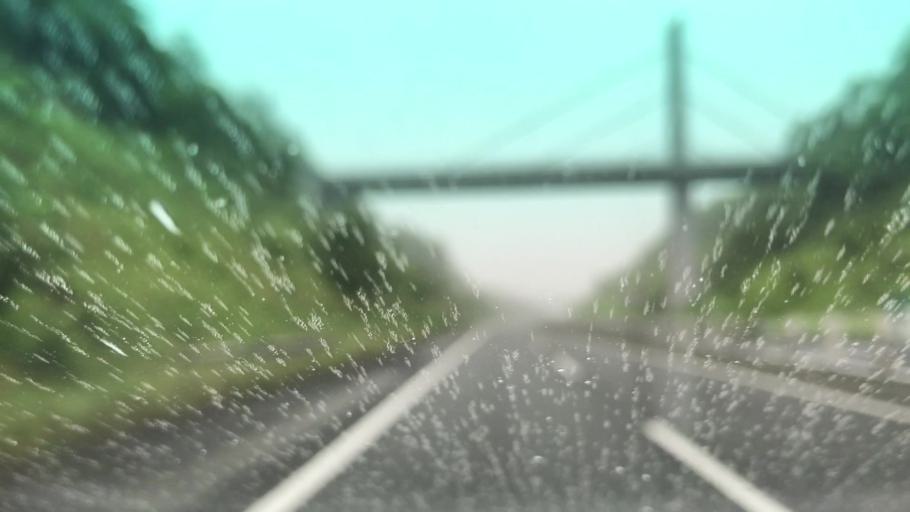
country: JP
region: Hokkaido
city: Tomakomai
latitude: 42.6256
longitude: 141.4820
